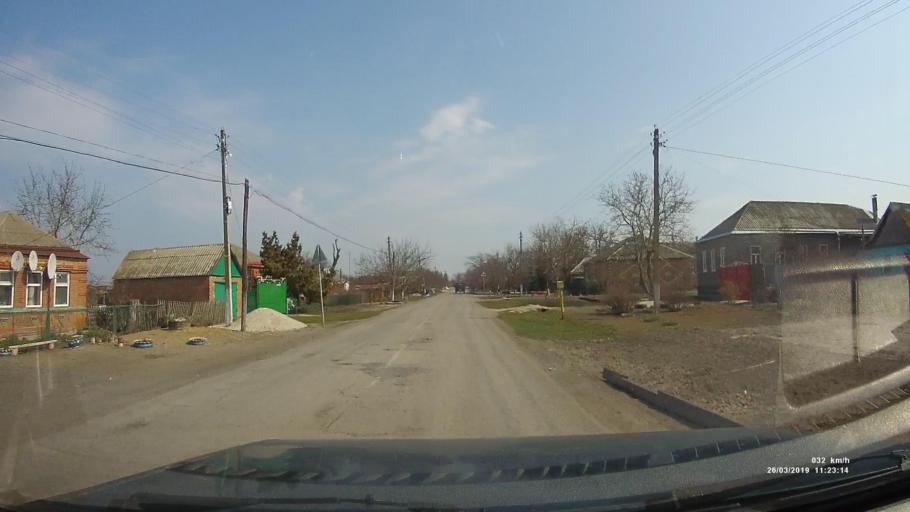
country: RU
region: Rostov
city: Novobessergenovka
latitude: 47.1397
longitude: 38.5587
